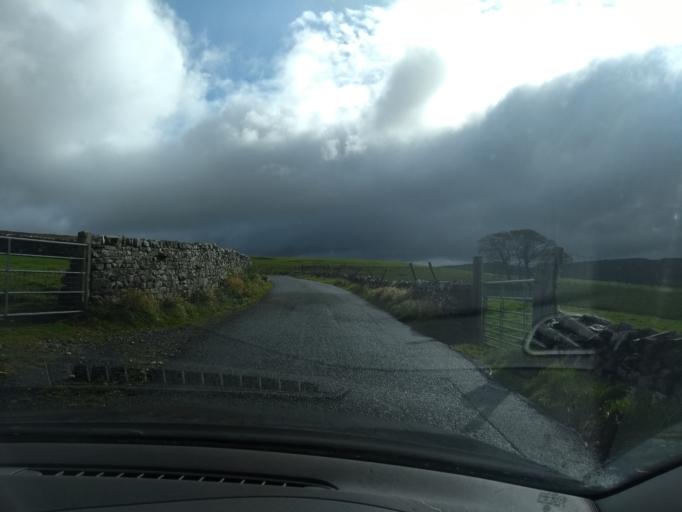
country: GB
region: England
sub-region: North Yorkshire
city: Settle
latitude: 54.1038
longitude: -2.2266
